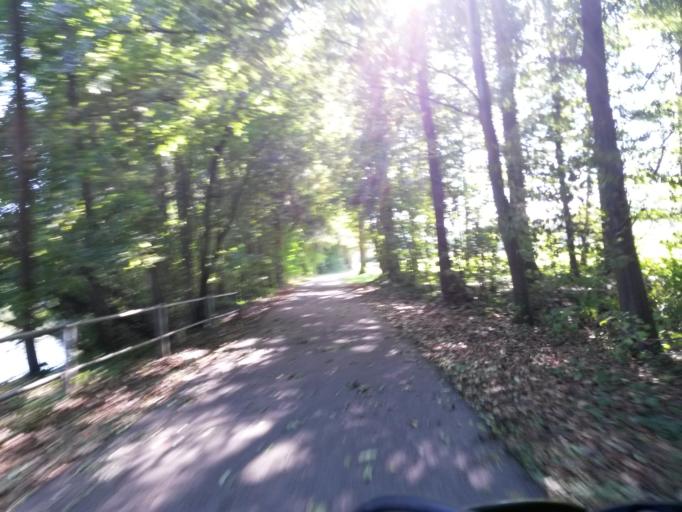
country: DE
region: Baden-Wuerttemberg
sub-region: Regierungsbezirk Stuttgart
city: Markgroningen
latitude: 48.9411
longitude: 9.0800
